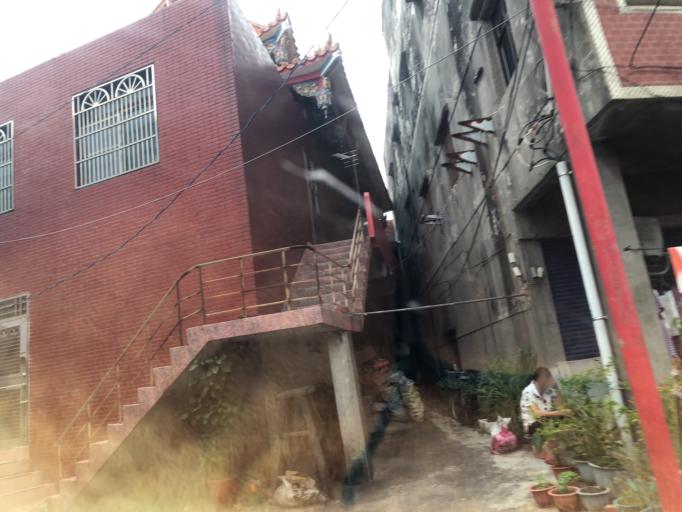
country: TW
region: Taiwan
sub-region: Chiayi
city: Taibao
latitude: 23.7217
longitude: 120.2103
